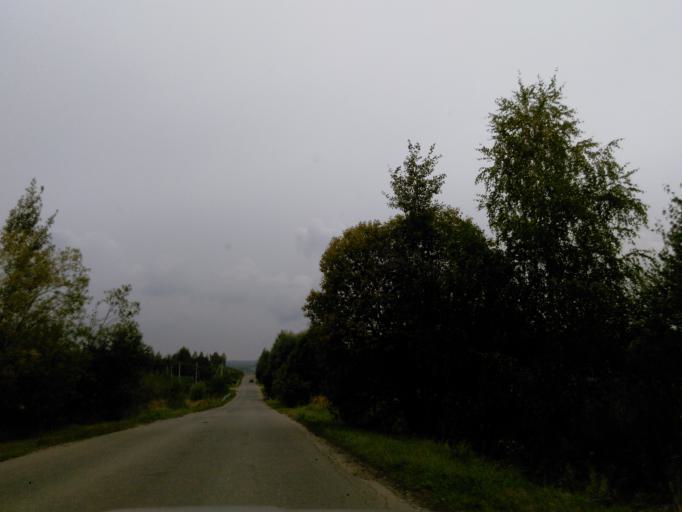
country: RU
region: Moskovskaya
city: Mendeleyevo
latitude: 56.1060
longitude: 37.2544
